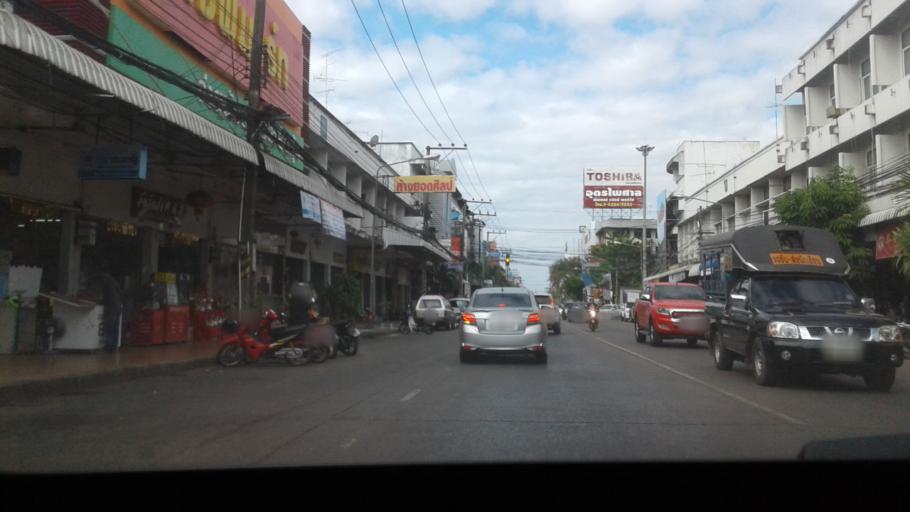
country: TH
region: Changwat Udon Thani
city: Udon Thani
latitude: 17.4058
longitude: 102.7911
